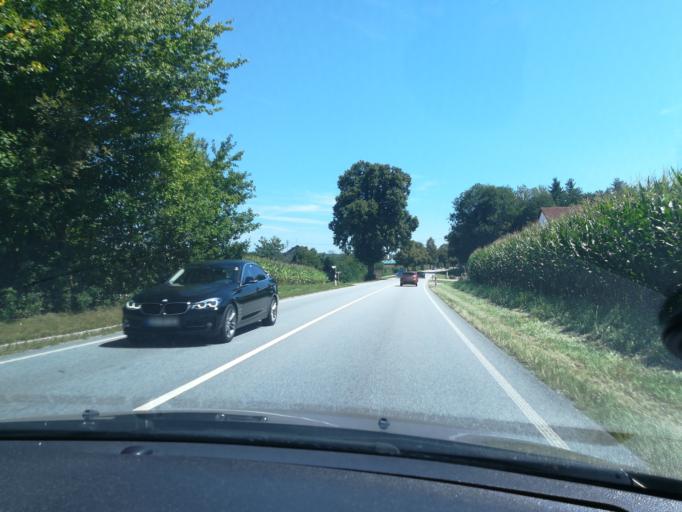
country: DE
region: Bavaria
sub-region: Upper Bavaria
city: Hohenlinden
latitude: 48.1566
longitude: 11.9712
